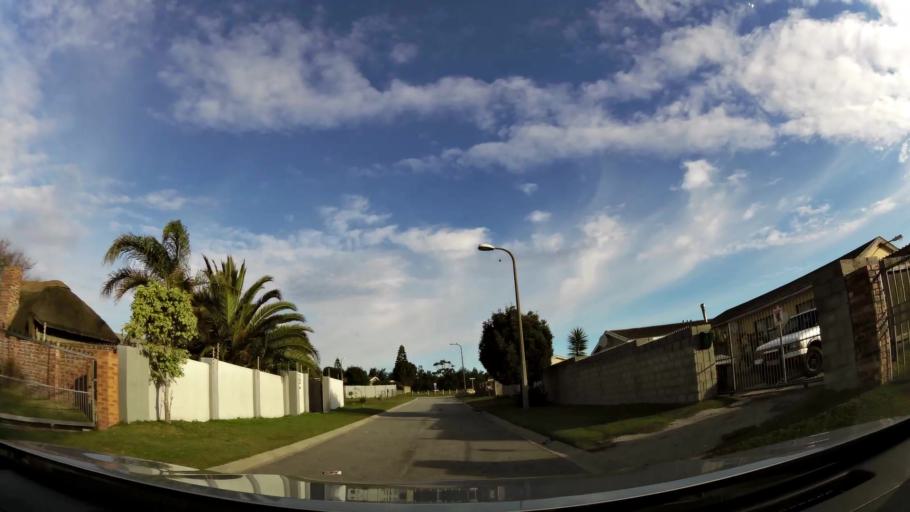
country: ZA
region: Eastern Cape
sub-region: Nelson Mandela Bay Metropolitan Municipality
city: Port Elizabeth
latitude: -33.9639
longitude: 25.4737
